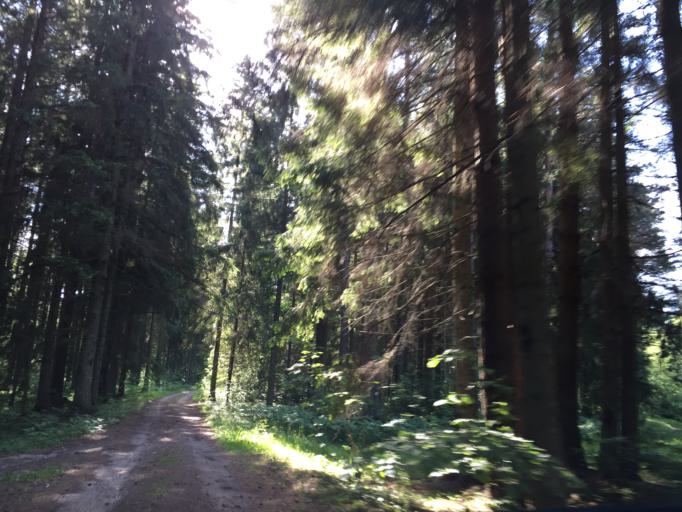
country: LV
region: Tukuma Rajons
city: Tukums
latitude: 57.0313
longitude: 23.2285
